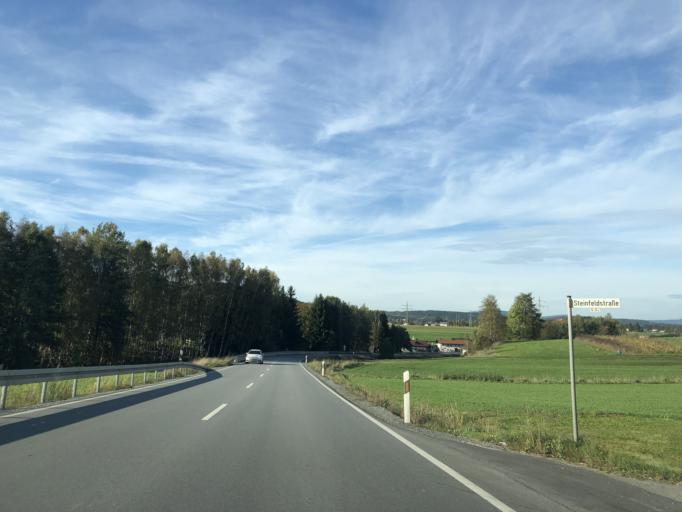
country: DE
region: Bavaria
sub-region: Lower Bavaria
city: Ruhmannsfelden
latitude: 48.9978
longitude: 12.9810
